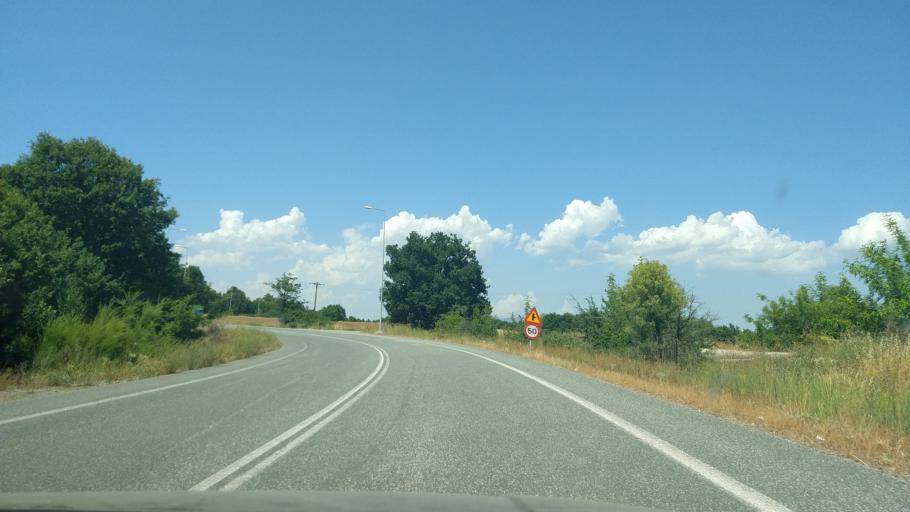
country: GR
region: West Macedonia
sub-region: Nomos Grevenon
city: Grevena
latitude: 40.0641
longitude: 21.4694
